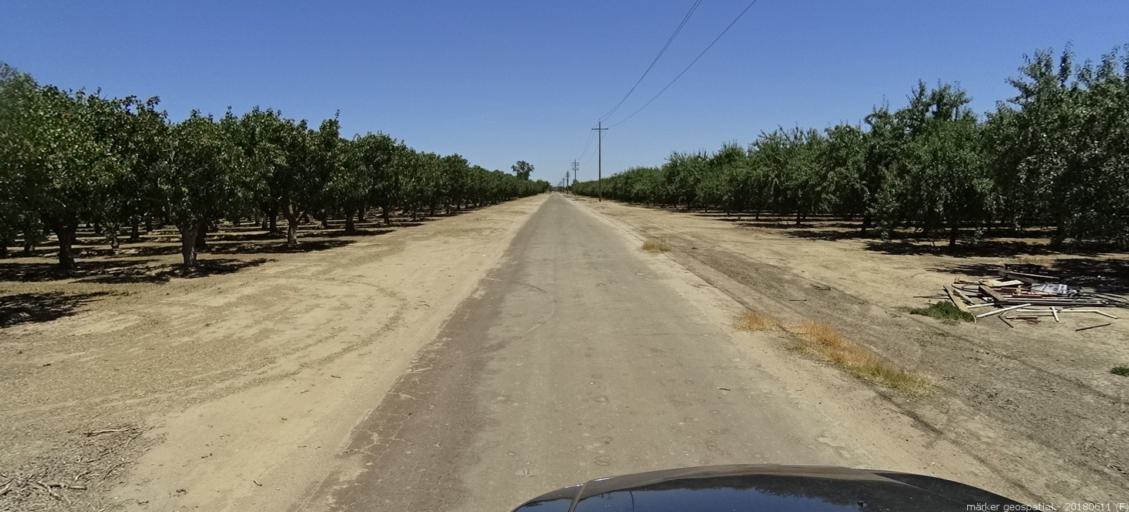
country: US
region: California
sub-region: Madera County
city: Fairmead
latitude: 37.0692
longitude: -120.2191
